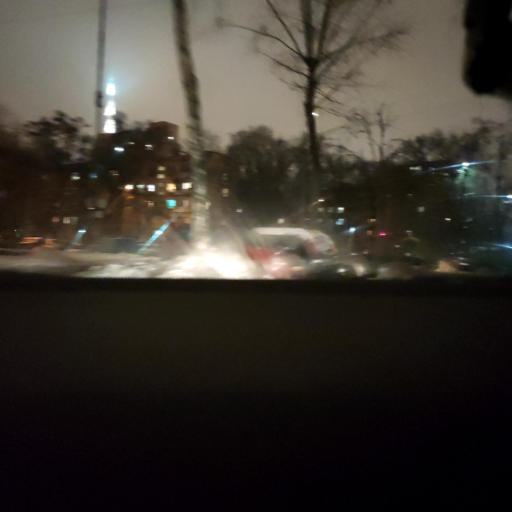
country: RU
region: Moskovskaya
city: Khoroshevo-Mnevniki
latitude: 55.7760
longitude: 37.4820
